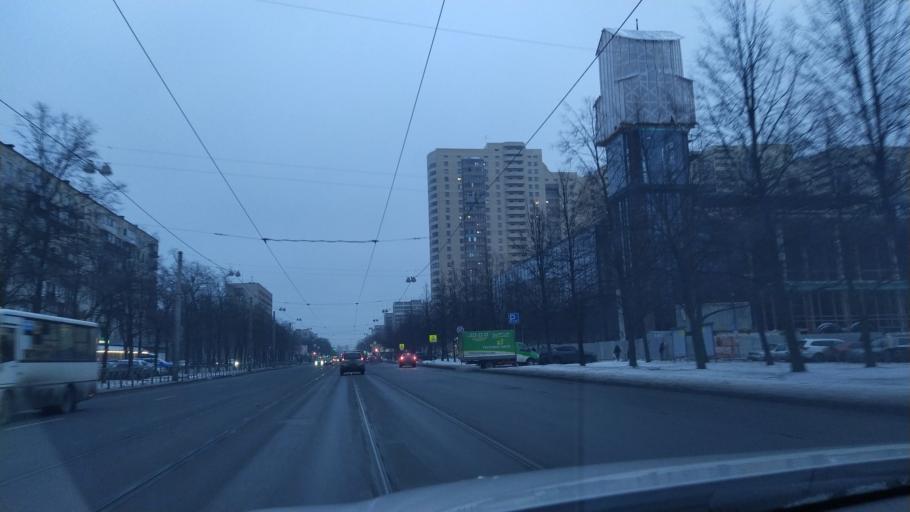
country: RU
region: Leningrad
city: Akademicheskoe
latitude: 60.0121
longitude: 30.4015
